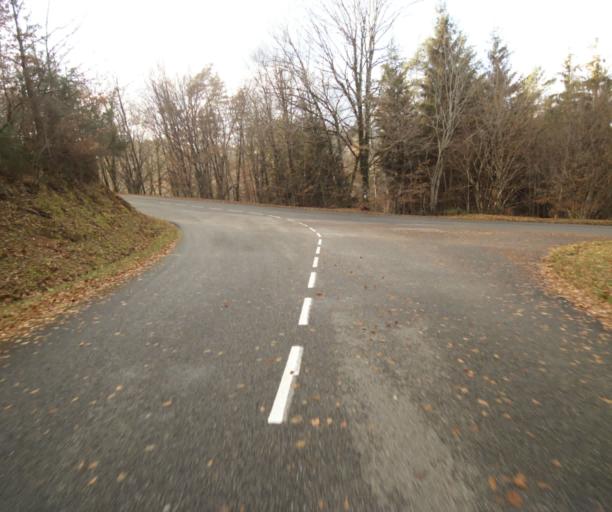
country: FR
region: Limousin
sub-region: Departement de la Correze
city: Laguenne
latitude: 45.2403
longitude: 1.7785
